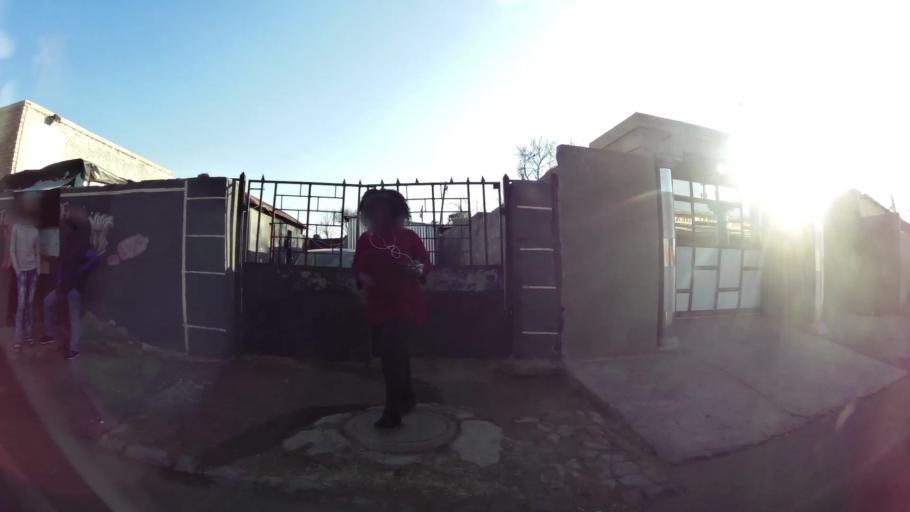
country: ZA
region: Gauteng
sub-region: City of Johannesburg Metropolitan Municipality
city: Soweto
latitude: -26.2524
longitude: 27.8839
